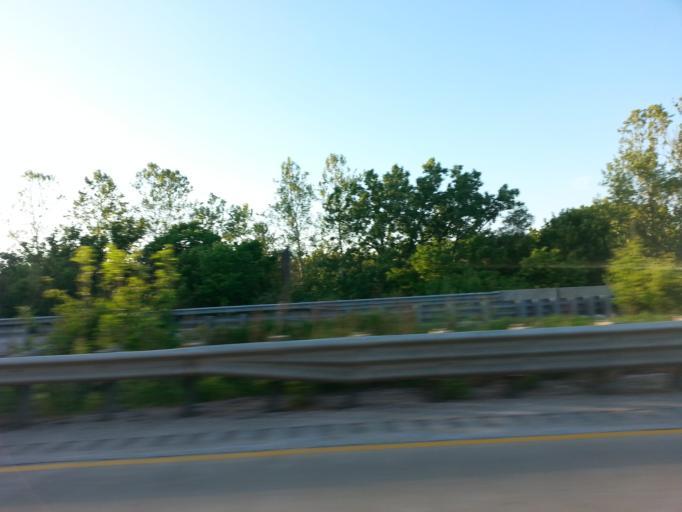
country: US
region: Illinois
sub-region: Vermilion County
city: Danville
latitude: 40.1142
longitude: -87.6015
